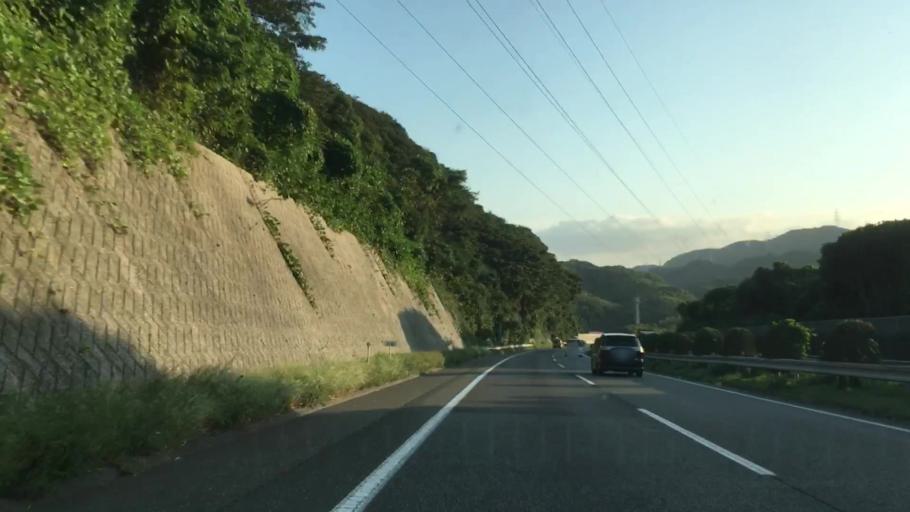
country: JP
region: Yamaguchi
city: Shimonoseki
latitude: 33.9120
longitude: 130.9756
